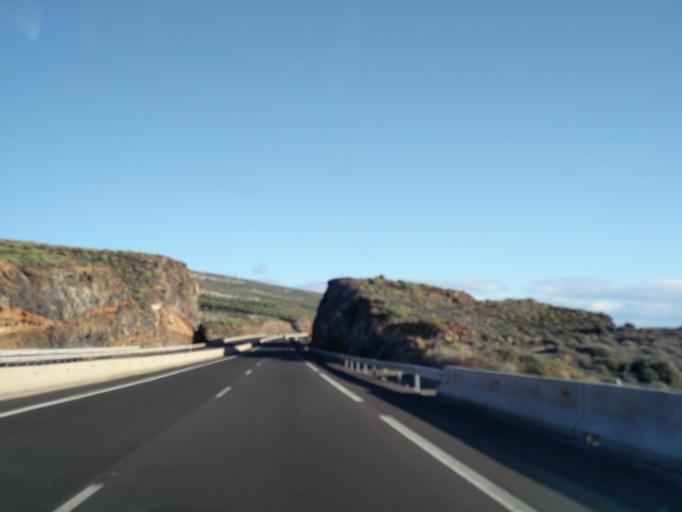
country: ES
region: Canary Islands
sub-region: Provincia de Santa Cruz de Tenerife
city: Fasnia
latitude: 28.2311
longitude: -16.4093
